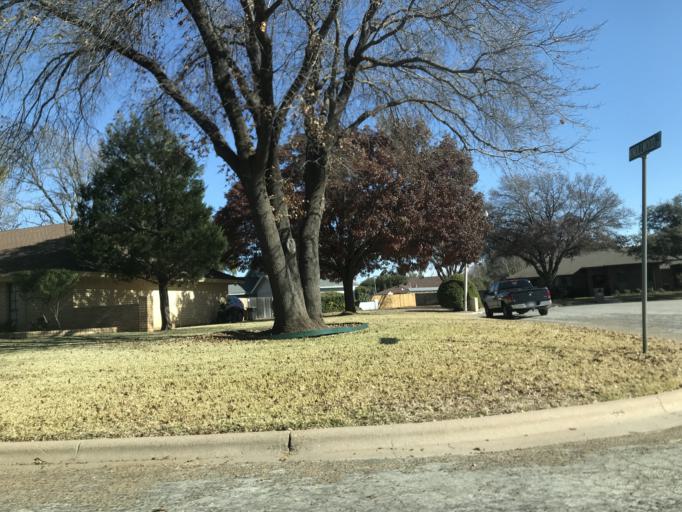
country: US
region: Texas
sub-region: Taylor County
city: Abilene
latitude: 32.3827
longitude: -99.7591
